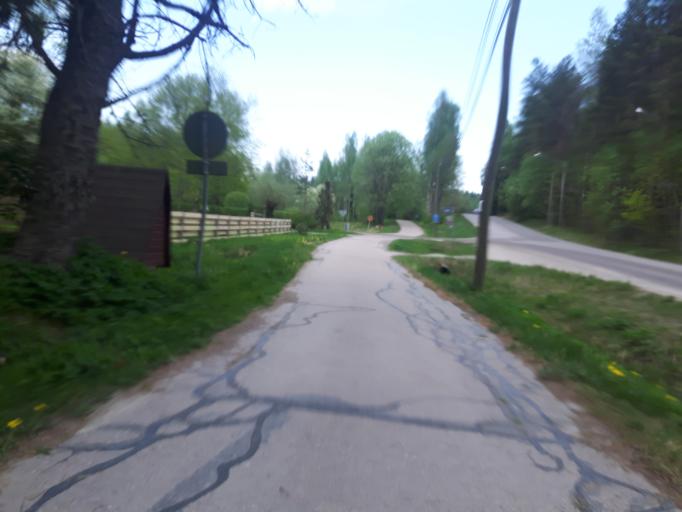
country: FI
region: Uusimaa
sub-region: Porvoo
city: Porvoo
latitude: 60.4013
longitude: 25.7235
